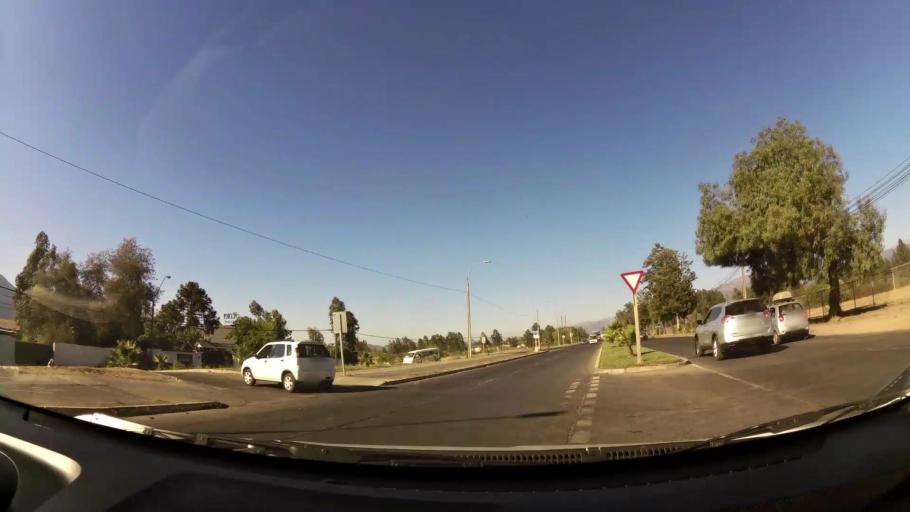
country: CL
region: O'Higgins
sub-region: Provincia de Colchagua
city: Chimbarongo
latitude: -34.5816
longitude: -70.9813
